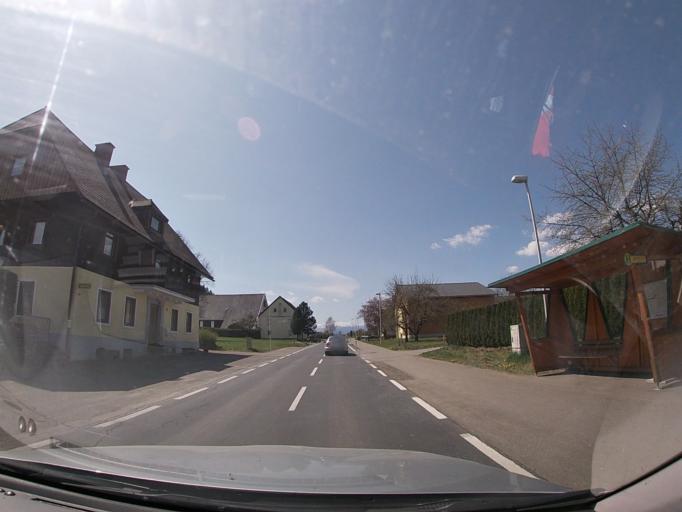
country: AT
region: Styria
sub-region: Politischer Bezirk Murtal
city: Sankt Margarethen bei Knittelfeld
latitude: 47.2332
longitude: 14.8671
